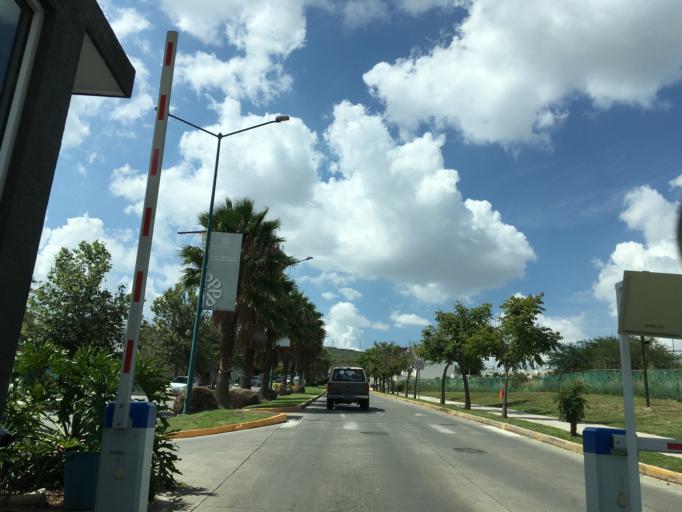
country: MX
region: Jalisco
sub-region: Tlajomulco de Zuniga
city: Altus Bosques
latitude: 20.5830
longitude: -103.3656
